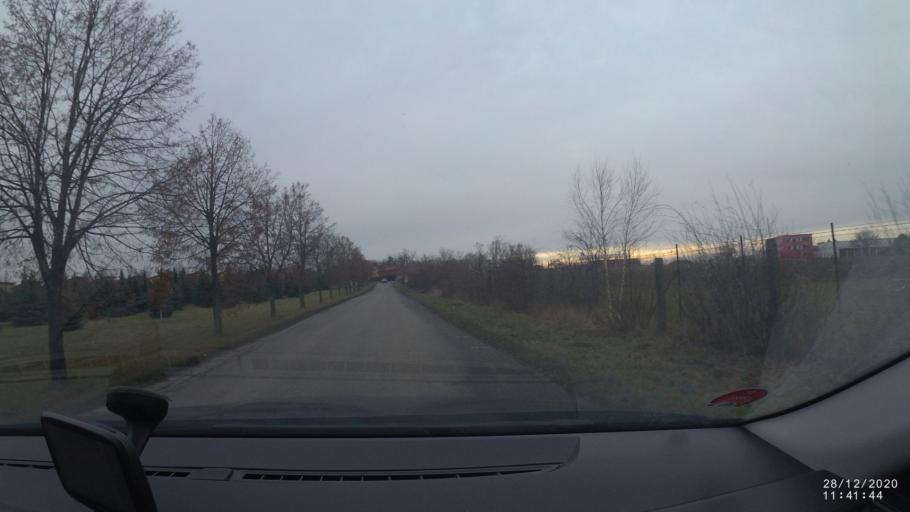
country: CZ
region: Central Bohemia
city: Zelenec
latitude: 50.1396
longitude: 14.6582
